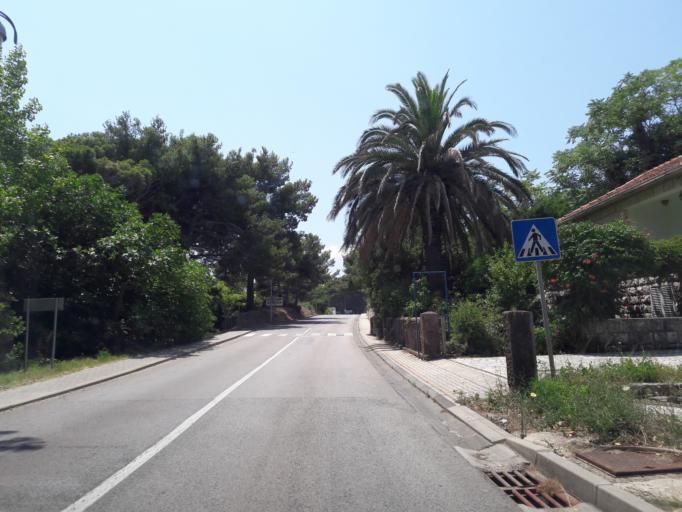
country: HR
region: Dubrovacko-Neretvanska
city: Orebic
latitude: 42.9790
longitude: 17.1924
